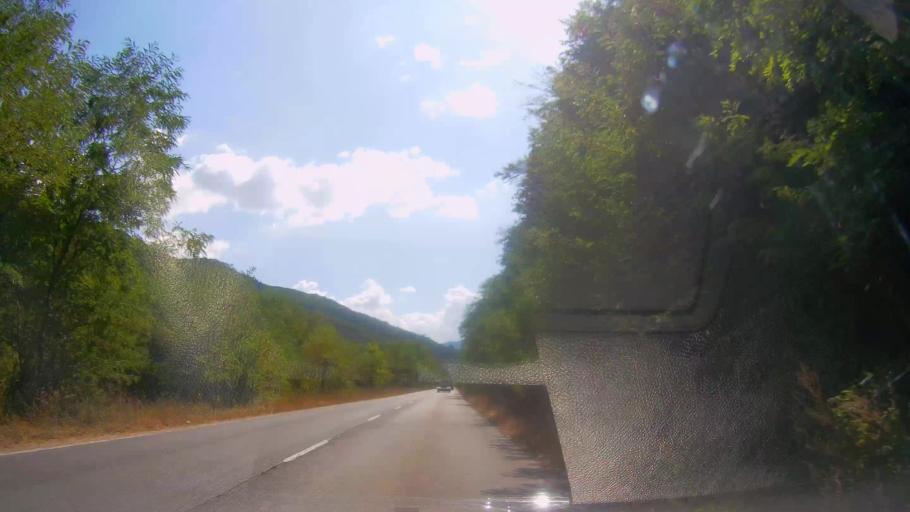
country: BG
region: Stara Zagora
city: Gurkovo
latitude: 42.7569
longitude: 25.7081
